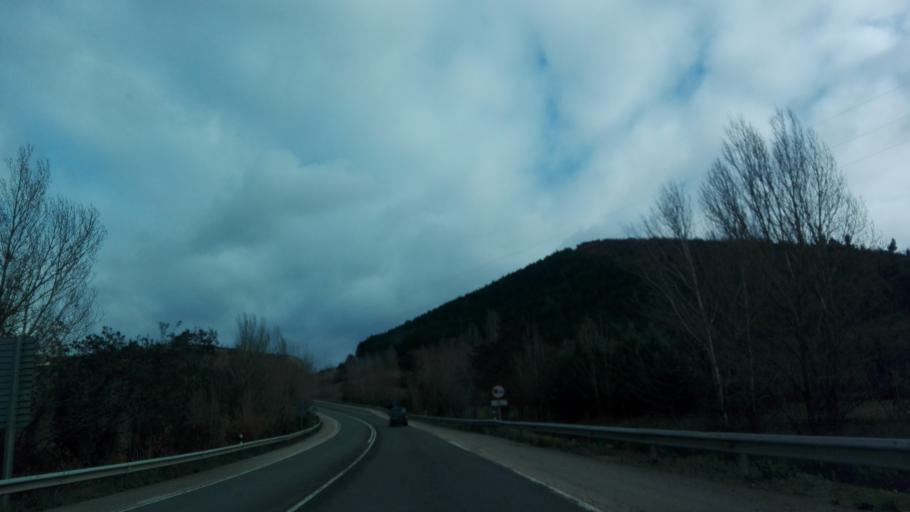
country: ES
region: Navarre
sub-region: Provincia de Navarra
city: Atarrabia
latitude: 42.8386
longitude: -1.6061
